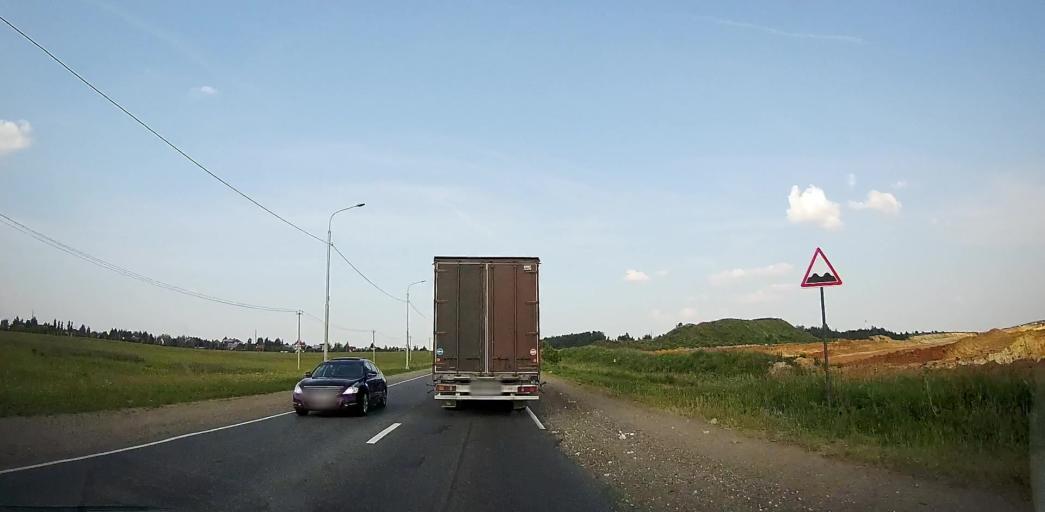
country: RU
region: Moskovskaya
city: Ostrovtsy
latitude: 55.5435
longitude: 38.0566
